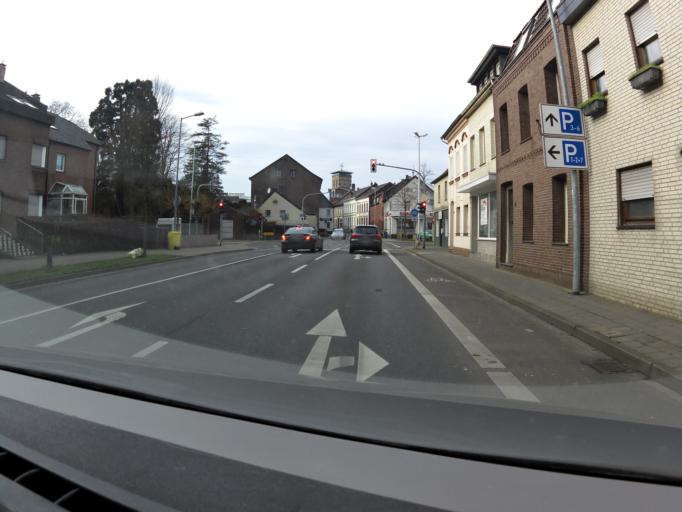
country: DE
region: North Rhine-Westphalia
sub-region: Regierungsbezirk Dusseldorf
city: Nettetal
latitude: 51.2970
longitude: 6.2506
